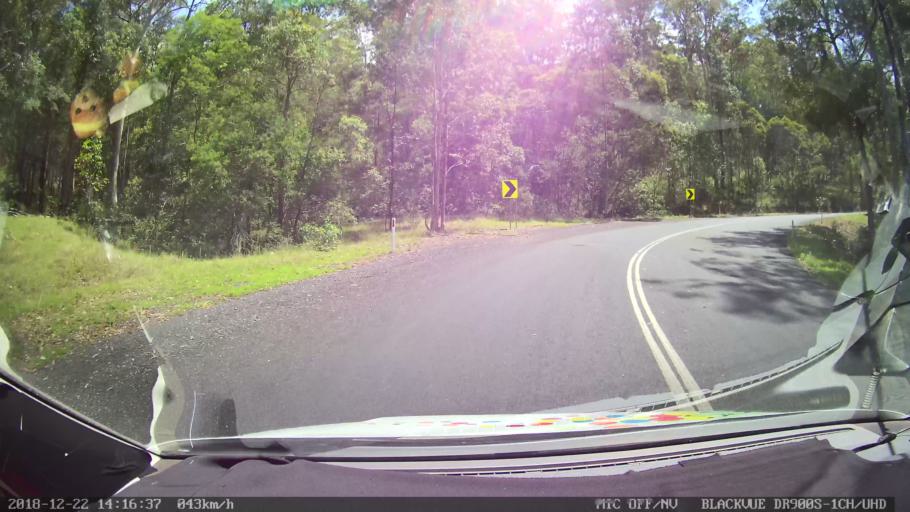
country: AU
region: New South Wales
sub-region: Clarence Valley
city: Coutts Crossing
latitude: -30.0062
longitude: 152.6716
